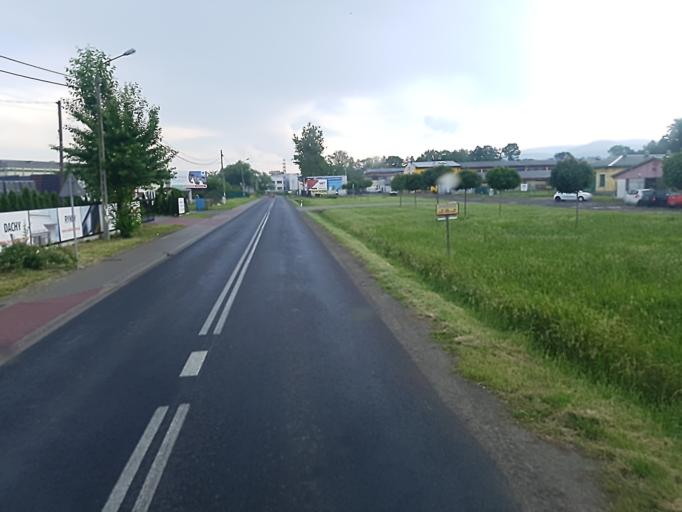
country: PL
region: Silesian Voivodeship
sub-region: Powiat bielski
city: Mazancowice
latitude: 49.8460
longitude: 18.9931
